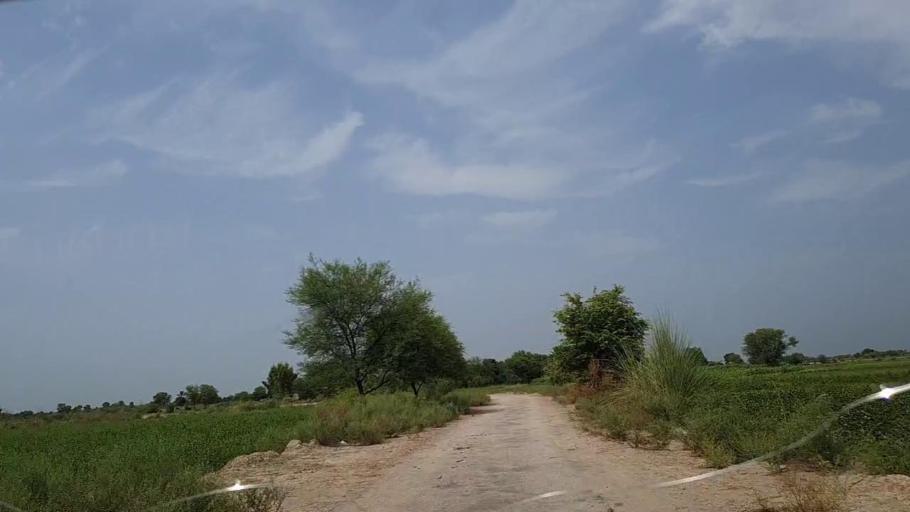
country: PK
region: Sindh
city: Tharu Shah
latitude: 26.9013
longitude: 68.0752
